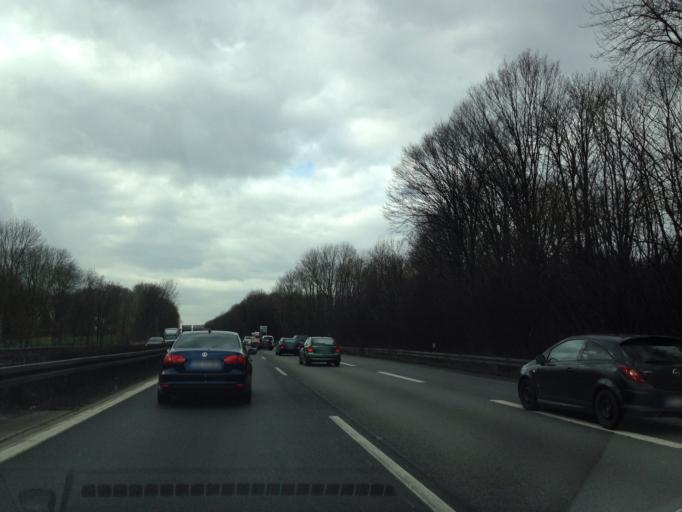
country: DE
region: North Rhine-Westphalia
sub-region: Regierungsbezirk Arnsberg
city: Bochum
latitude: 51.5043
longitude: 7.2563
